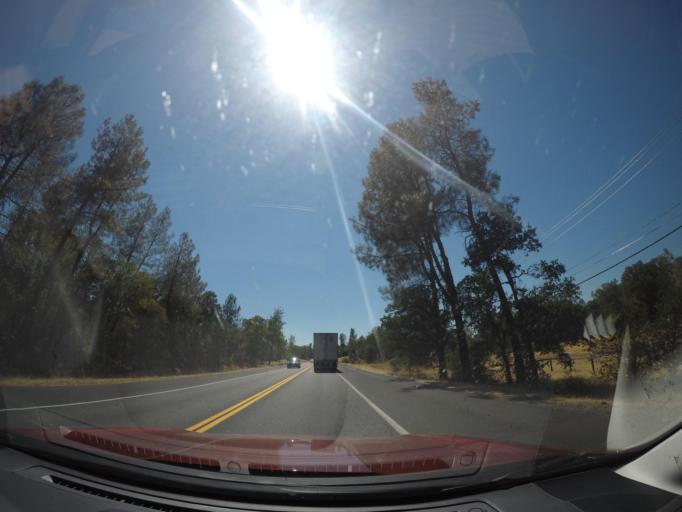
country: US
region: California
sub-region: Shasta County
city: Bella Vista
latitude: 40.6272
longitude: -122.2892
